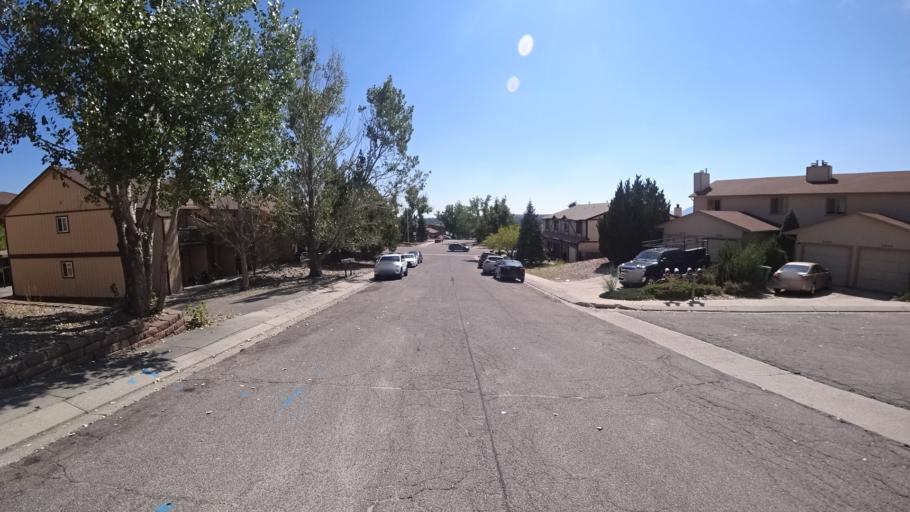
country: US
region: Colorado
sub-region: El Paso County
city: Colorado Springs
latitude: 38.9110
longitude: -104.7774
